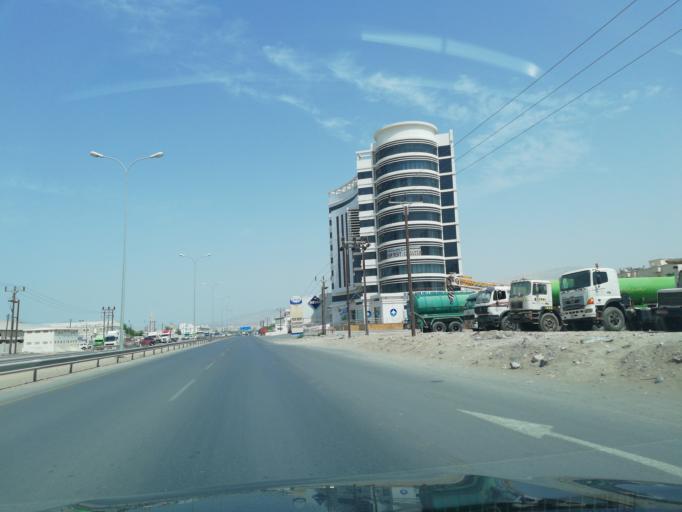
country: OM
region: Muhafazat Masqat
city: Bawshar
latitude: 23.5826
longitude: 58.3724
